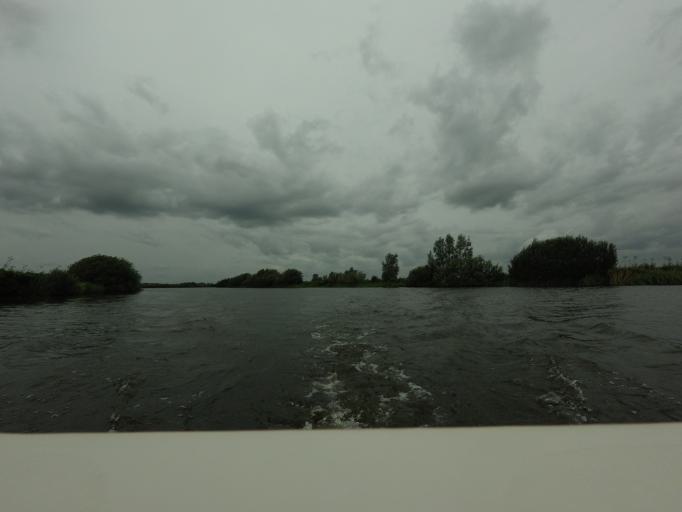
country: NL
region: Friesland
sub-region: Gemeente Boarnsterhim
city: Aldeboarn
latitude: 53.0960
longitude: 5.9207
